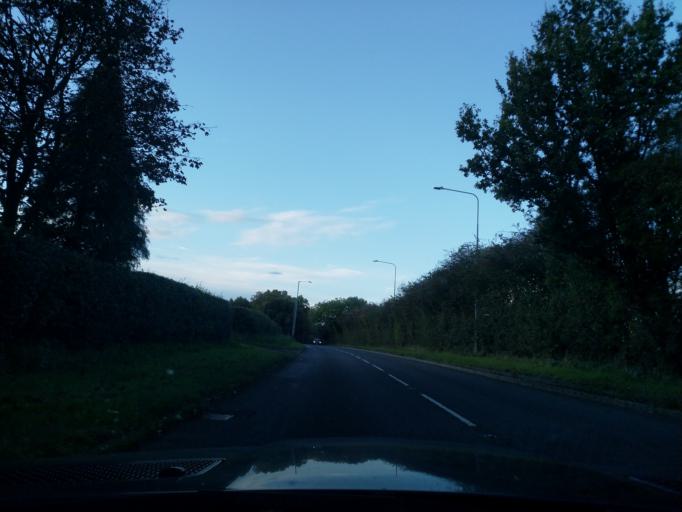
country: GB
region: England
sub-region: Warwickshire
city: Henley in Arden
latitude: 52.3382
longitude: -1.7729
